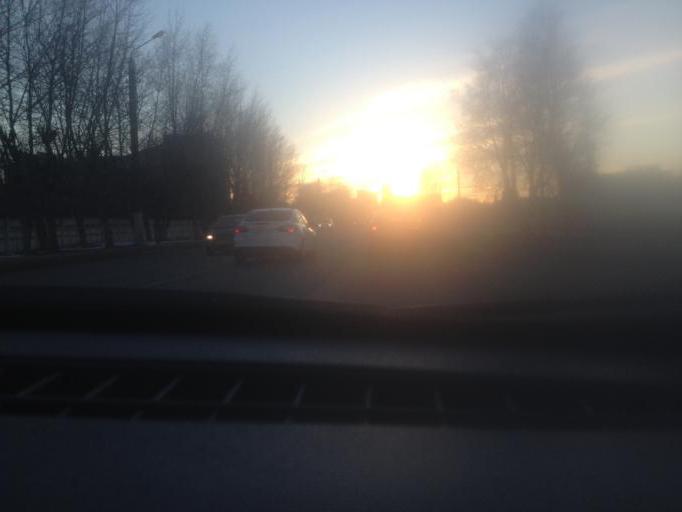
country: RU
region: Tula
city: Mendeleyevskiy
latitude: 54.1918
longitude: 37.5405
